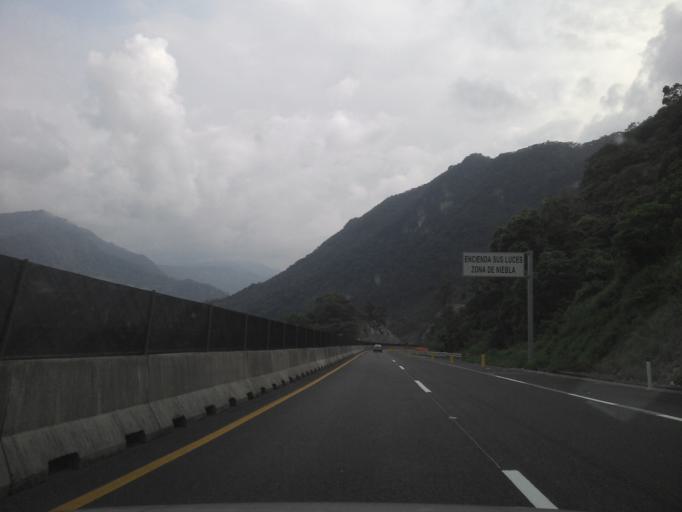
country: MX
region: Puebla
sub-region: Xicotepec
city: San Lorenzo
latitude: 20.3655
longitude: -97.9582
